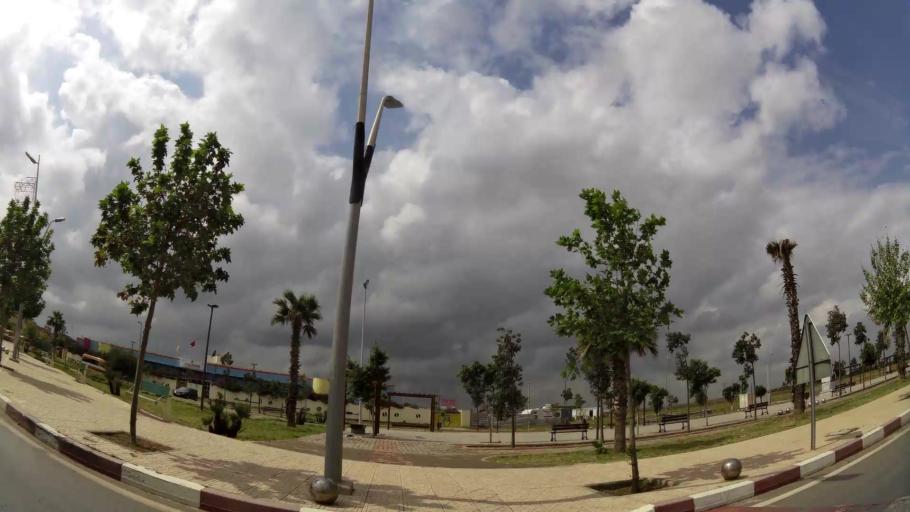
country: MA
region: Rabat-Sale-Zemmour-Zaer
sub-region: Khemisset
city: Tiflet
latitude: 33.8942
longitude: -6.3357
